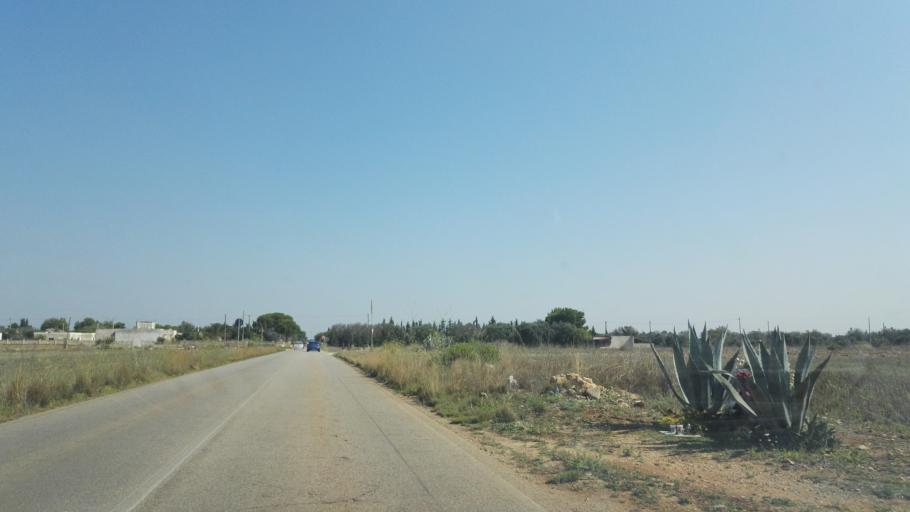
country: IT
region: Apulia
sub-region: Provincia di Lecce
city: Nardo
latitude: 40.1164
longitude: 18.0201
